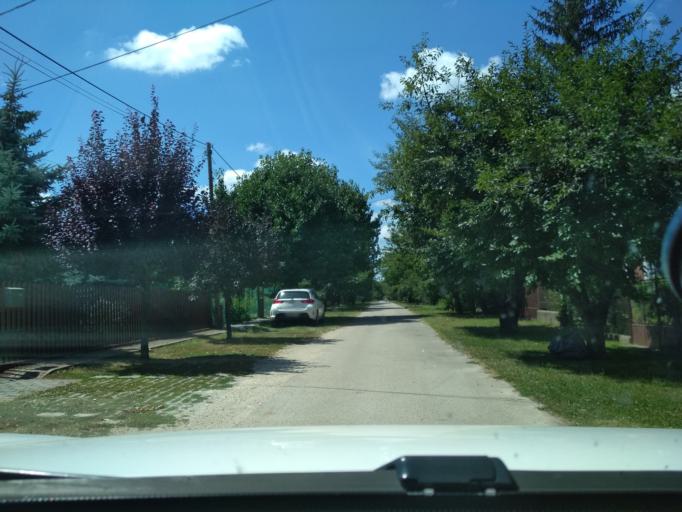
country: HU
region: Fejer
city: Gardony
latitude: 47.2143
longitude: 18.6593
